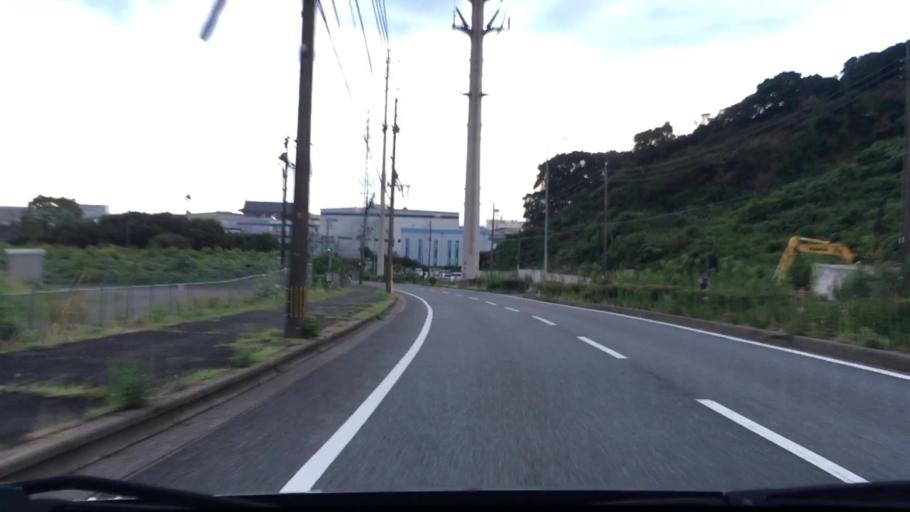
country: JP
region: Yamaguchi
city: Shimonoseki
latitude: 33.8869
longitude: 130.9822
